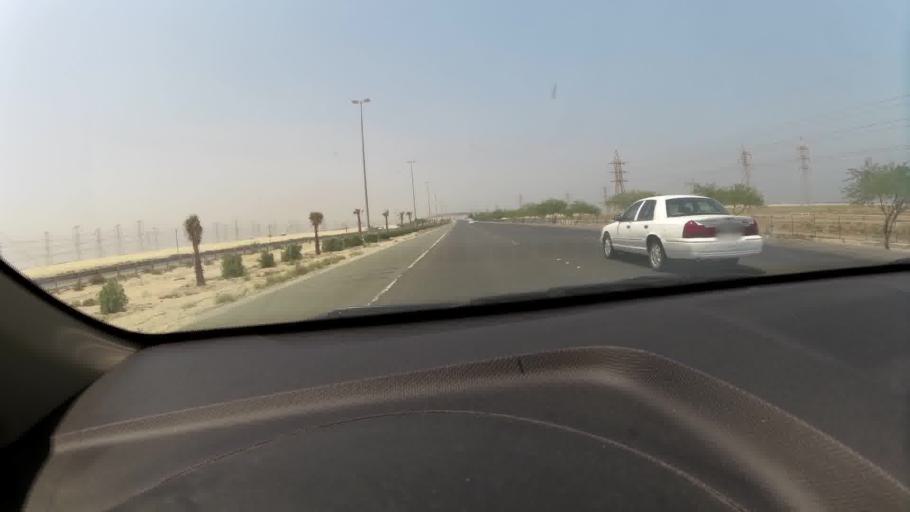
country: KW
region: Al Ahmadi
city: Al Fahahil
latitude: 28.8581
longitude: 48.2409
